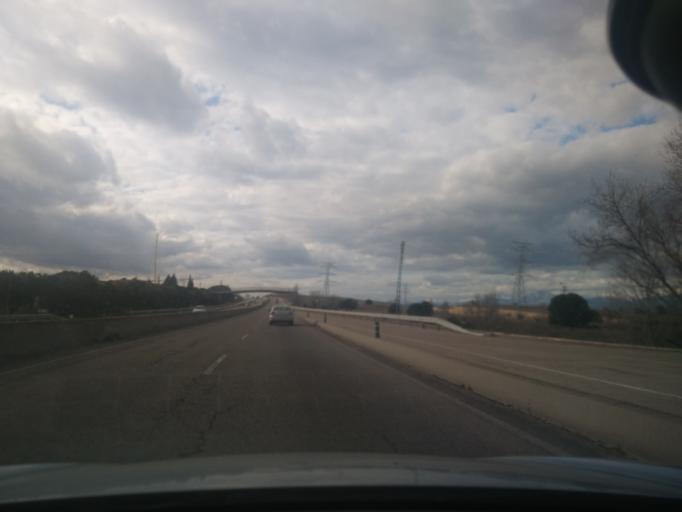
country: ES
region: Madrid
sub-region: Provincia de Madrid
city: Alcobendas
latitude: 40.5521
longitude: -3.6717
